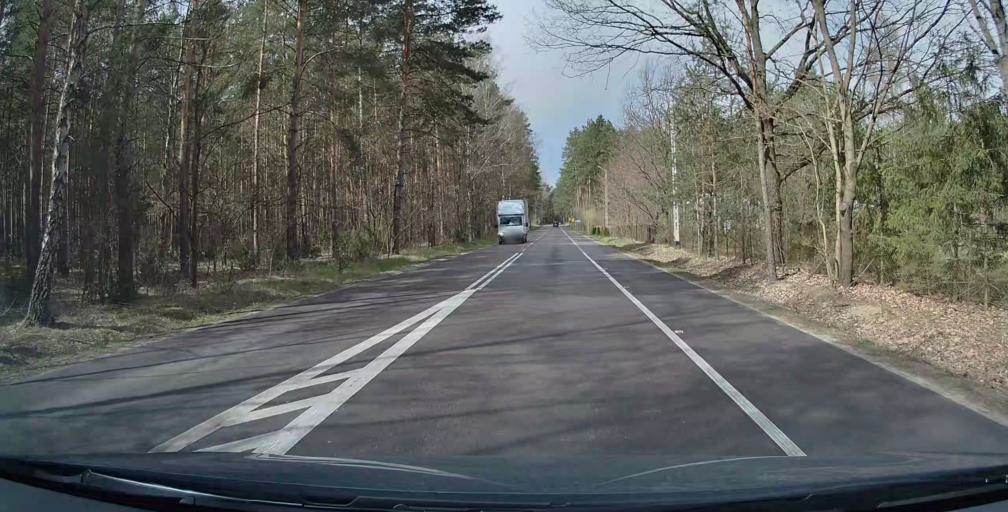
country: PL
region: Masovian Voivodeship
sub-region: Powiat wyszkowski
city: Dlugosiodlo
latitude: 52.7608
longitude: 21.5807
